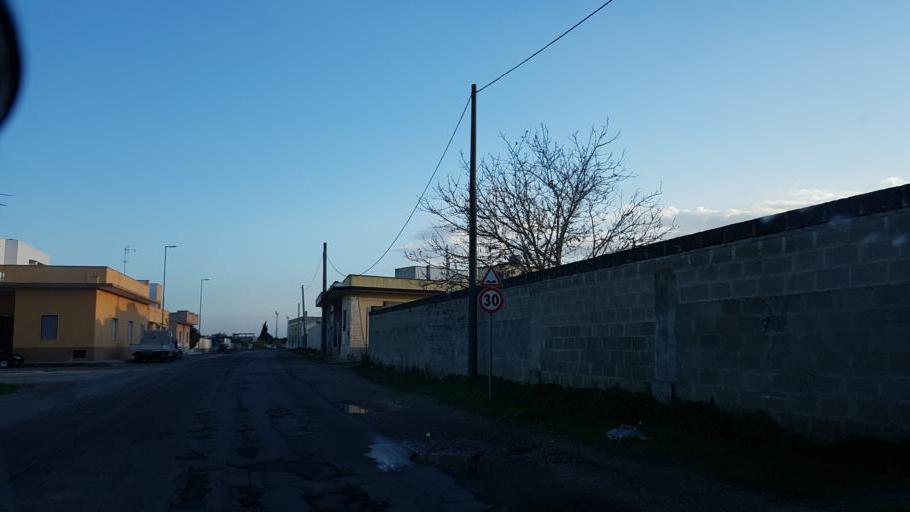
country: IT
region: Apulia
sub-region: Provincia di Lecce
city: Surbo
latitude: 40.3901
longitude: 18.1270
